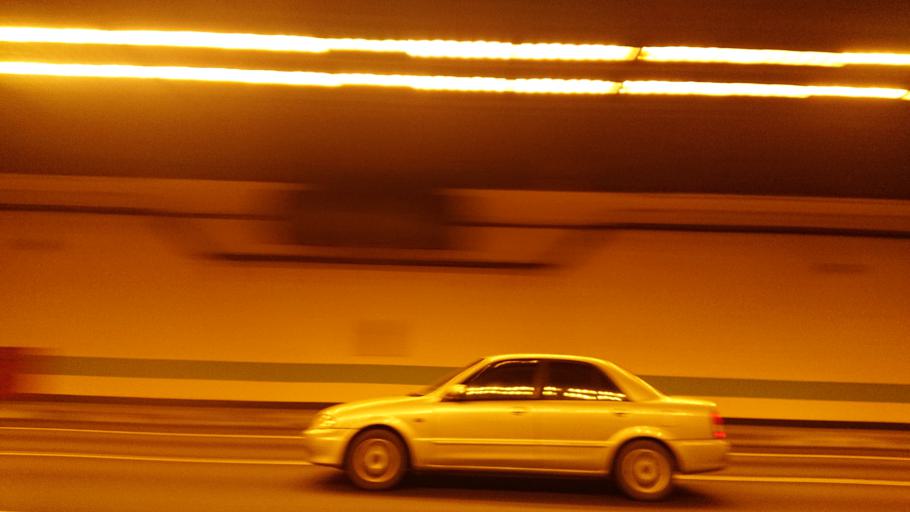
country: TW
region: Taiwan
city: Daxi
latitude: 24.9080
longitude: 121.2848
